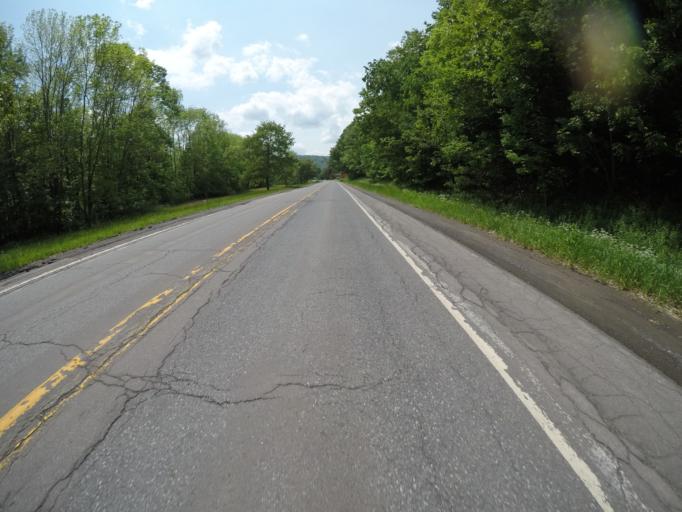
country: US
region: New York
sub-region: Delaware County
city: Stamford
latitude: 42.1509
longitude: -74.6326
